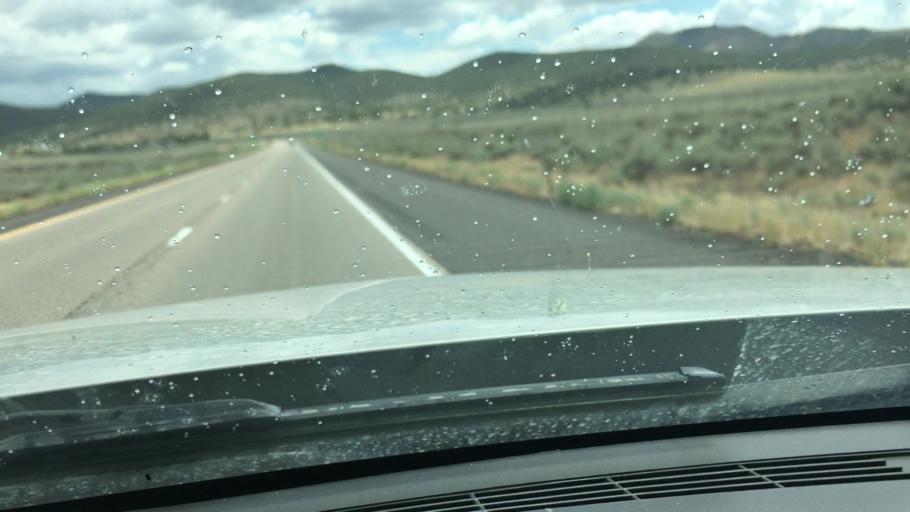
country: US
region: Utah
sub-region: Beaver County
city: Beaver
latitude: 38.2013
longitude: -112.6472
